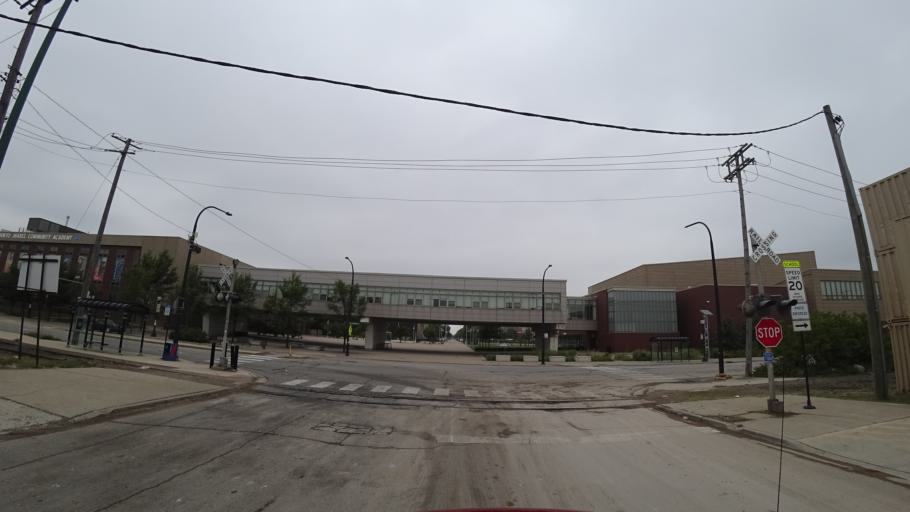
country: US
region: Illinois
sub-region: Cook County
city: Chicago
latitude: 41.8521
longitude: -87.6637
